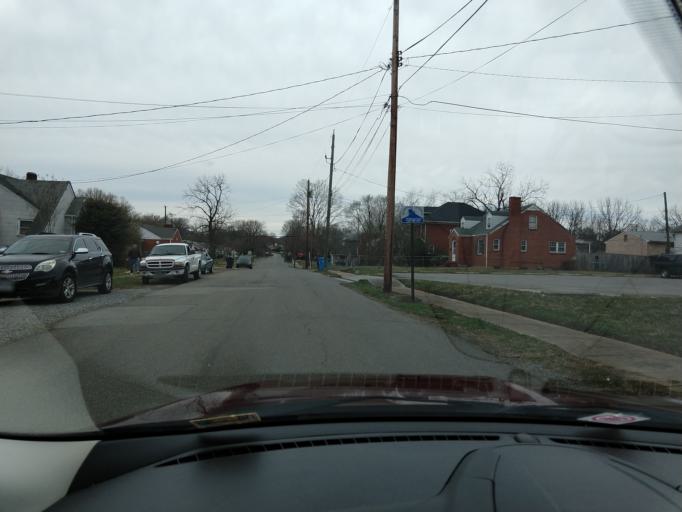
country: US
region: Virginia
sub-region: City of Roanoke
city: Roanoke
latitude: 37.3017
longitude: -79.9357
